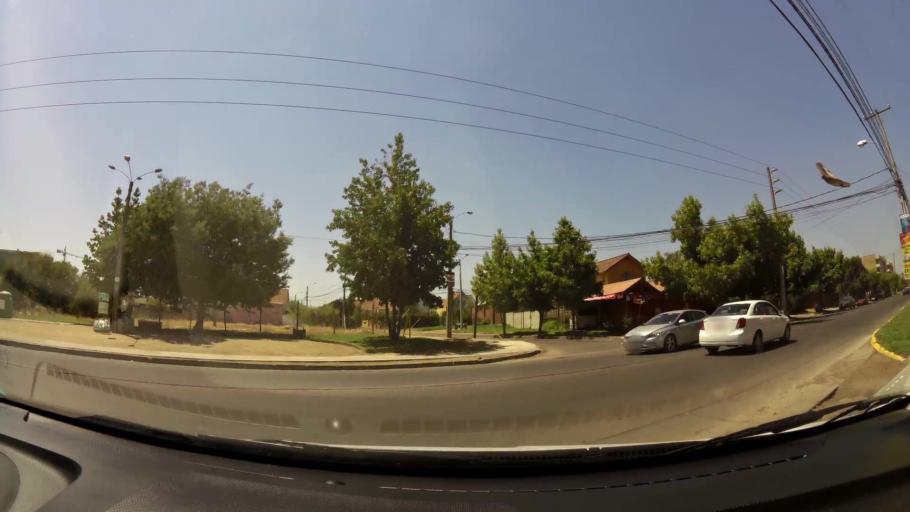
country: CL
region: Maule
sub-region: Provincia de Talca
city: Talca
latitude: -35.4321
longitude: -71.6256
